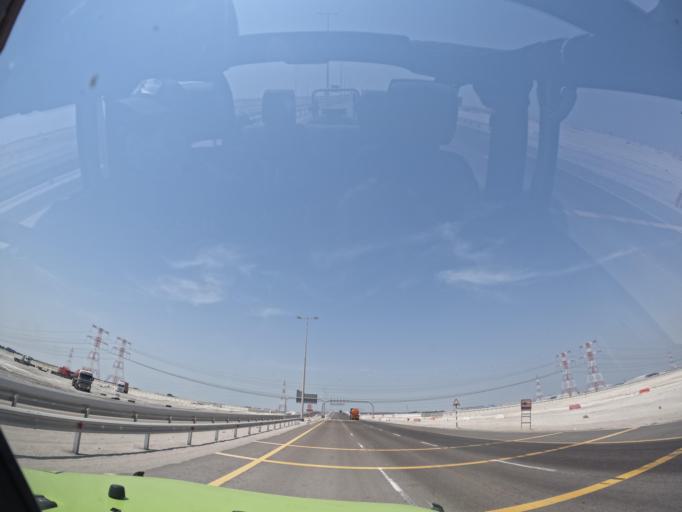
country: AE
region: Abu Dhabi
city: Abu Dhabi
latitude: 24.2523
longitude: 54.4673
